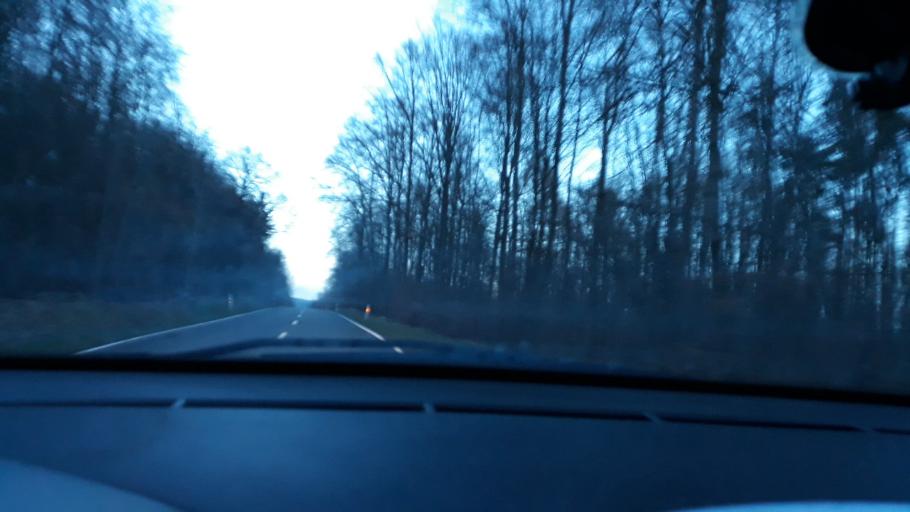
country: FR
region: Lorraine
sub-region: Departement de la Moselle
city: Sarreguemines
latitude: 49.1367
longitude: 7.0806
